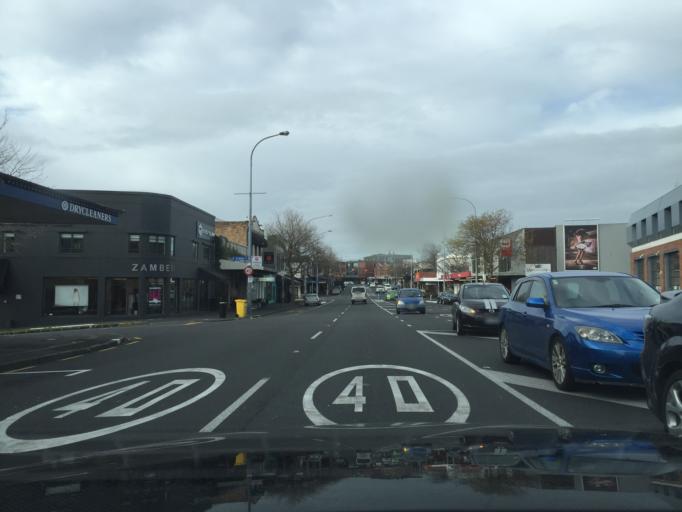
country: NZ
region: Auckland
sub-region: Auckland
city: Auckland
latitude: -36.8540
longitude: 174.7457
